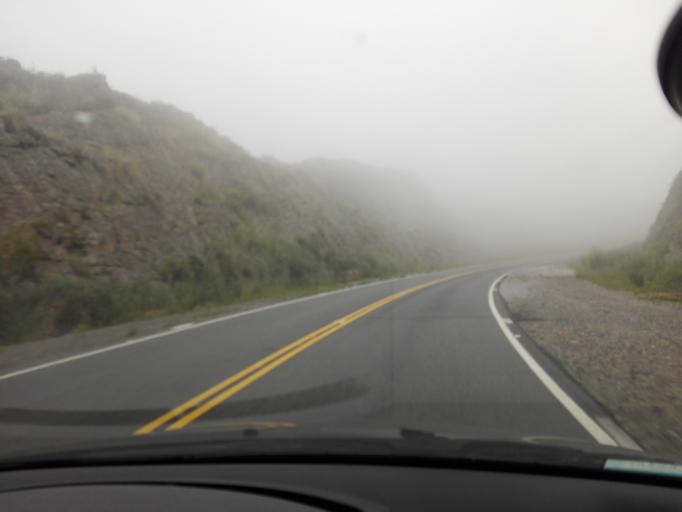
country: AR
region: Cordoba
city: Cuesta Blanca
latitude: -31.6011
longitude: -64.7101
